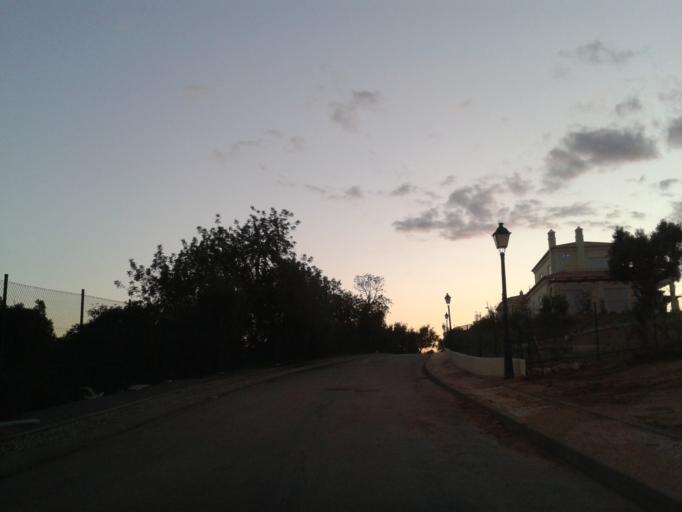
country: PT
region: Faro
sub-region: Lagoa
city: Estombar
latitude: 37.1283
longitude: -8.4783
